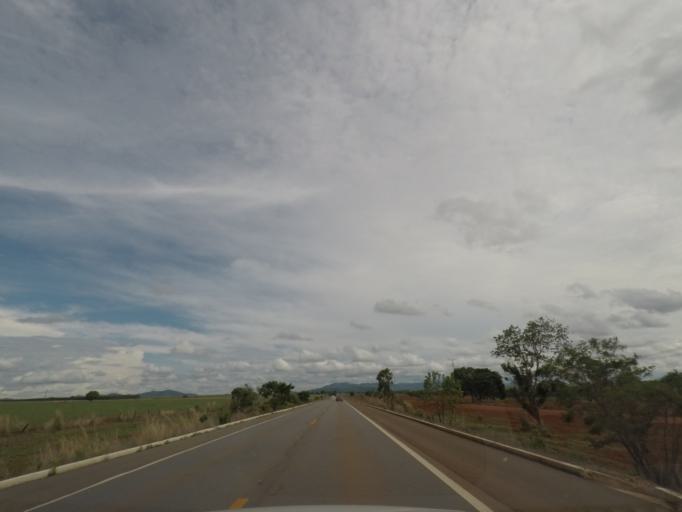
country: BR
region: Goias
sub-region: Barro Alto
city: Barro Alto
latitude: -14.8197
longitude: -49.0397
